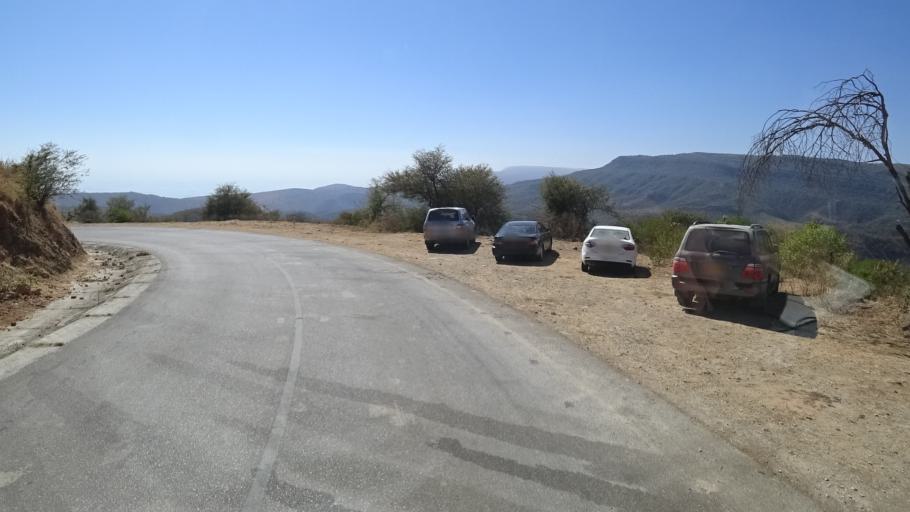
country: YE
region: Al Mahrah
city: Hawf
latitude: 16.7636
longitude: 53.3364
